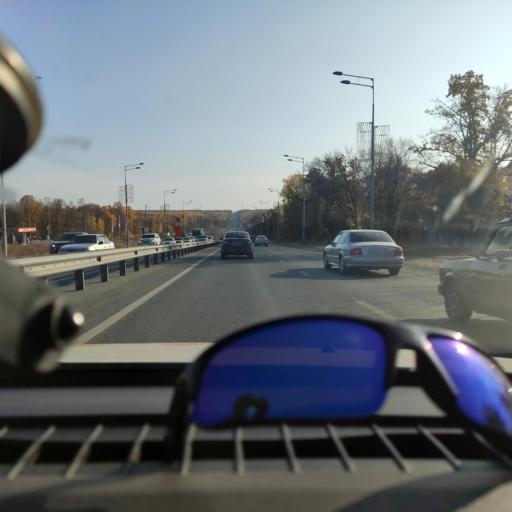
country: RU
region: Samara
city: Novosemeykino
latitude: 53.3452
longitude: 50.2332
